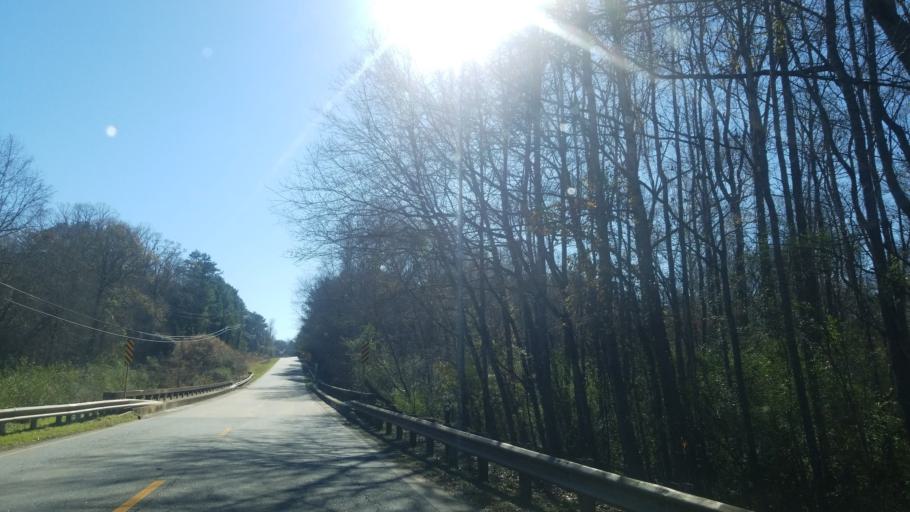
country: US
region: Alabama
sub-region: Lee County
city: Smiths Station
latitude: 32.5857
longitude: -85.0216
